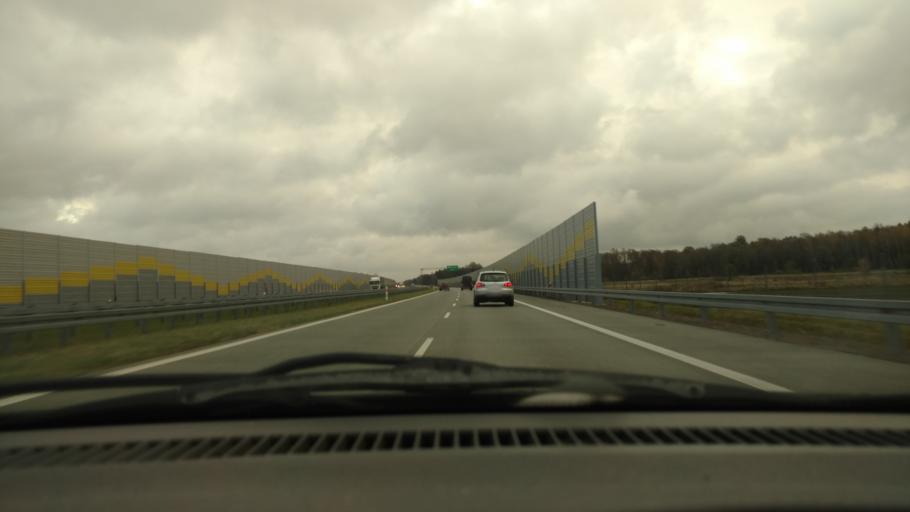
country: PL
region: Lodz Voivodeship
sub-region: Powiat lodzki wschodni
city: Rzgow
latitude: 51.6329
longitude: 19.4594
